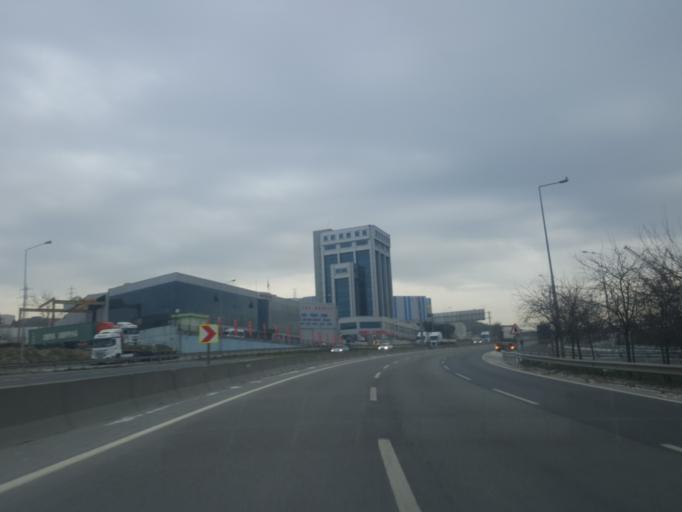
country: TR
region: Kocaeli
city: Tavsanli
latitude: 40.7920
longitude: 29.5270
